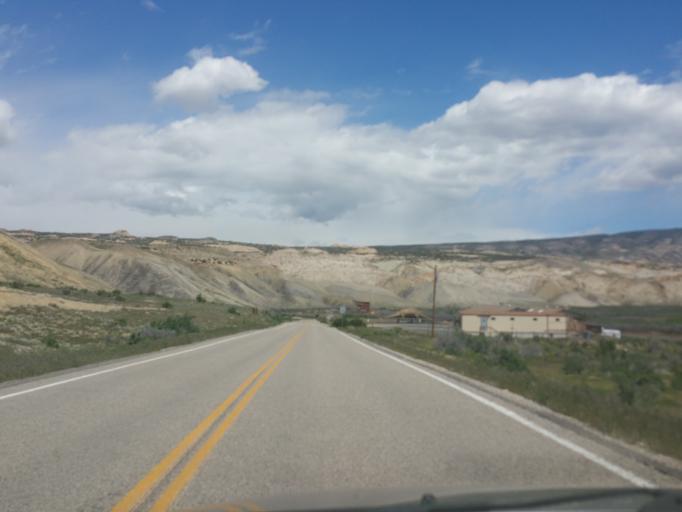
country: US
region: Utah
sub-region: Uintah County
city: Naples
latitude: 40.4257
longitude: -109.3347
